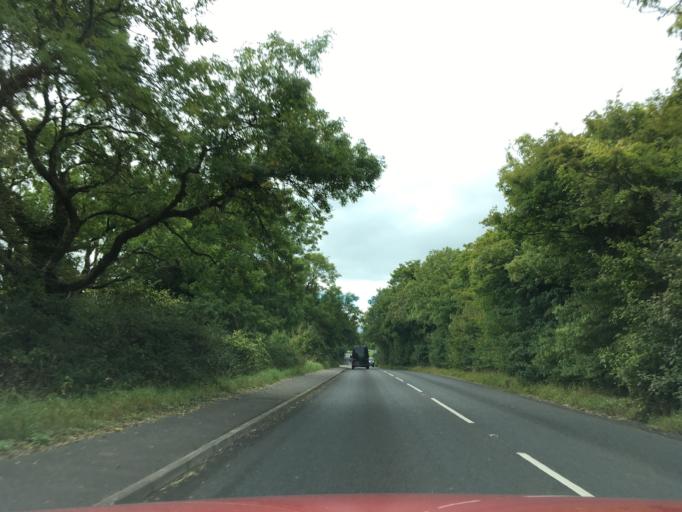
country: GB
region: England
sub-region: South Gloucestershire
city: Tytherington
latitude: 51.5980
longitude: -2.4932
